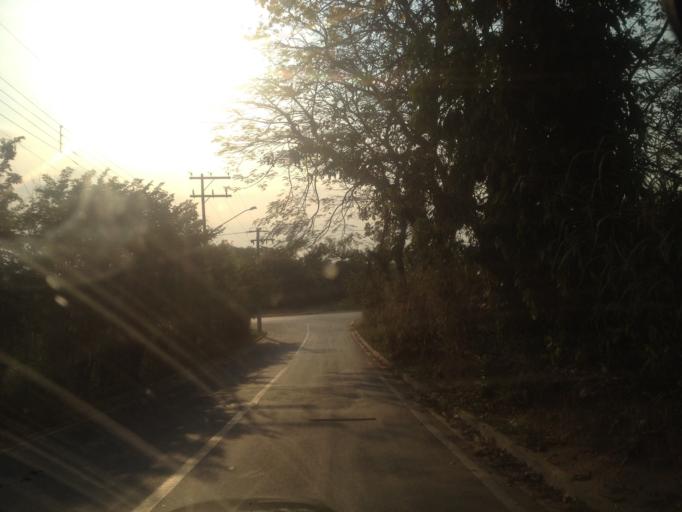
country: BR
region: Rio de Janeiro
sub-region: Porto Real
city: Porto Real
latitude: -22.4328
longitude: -44.3179
